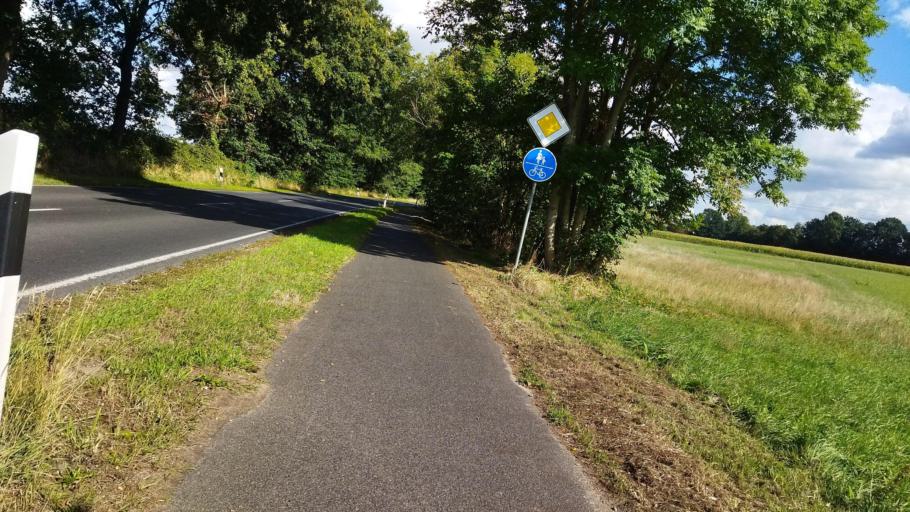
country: DE
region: Lower Saxony
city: Emsburen
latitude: 52.4010
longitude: 7.3219
